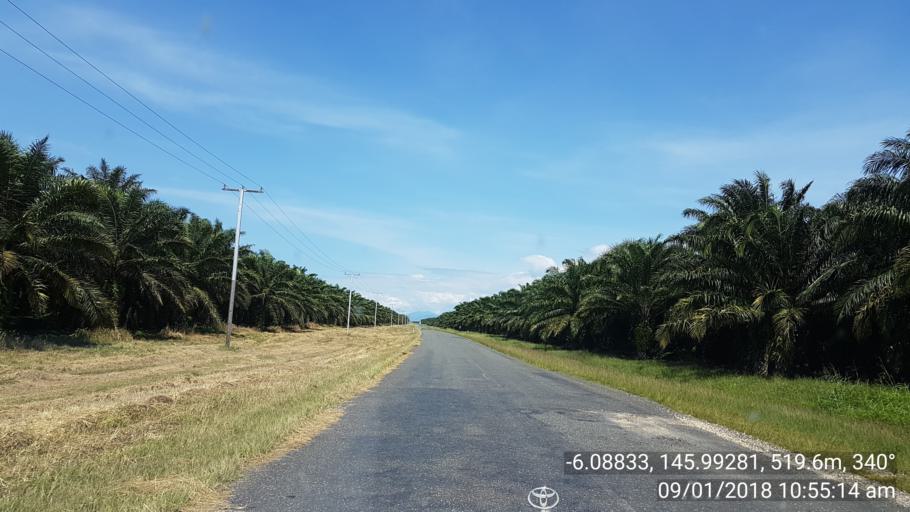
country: PG
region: Eastern Highlands
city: Kainantu
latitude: -6.0883
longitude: 145.9928
